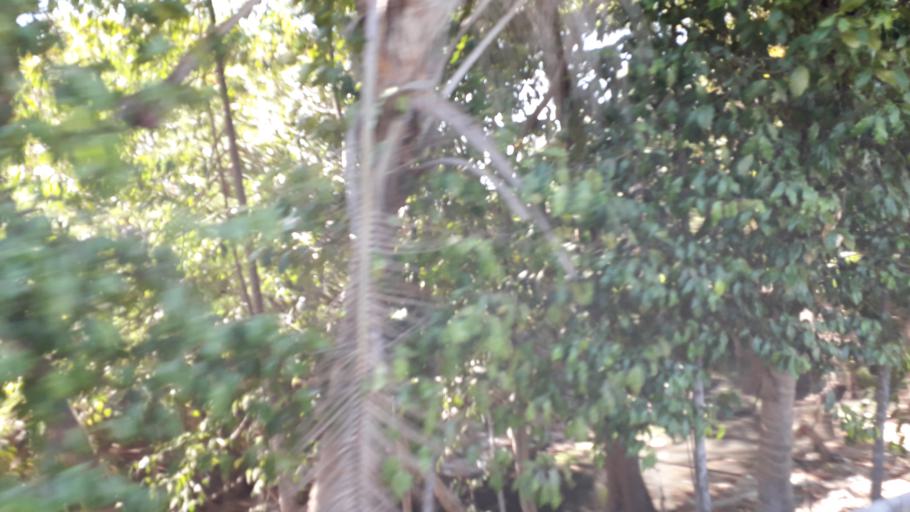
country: ID
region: Daerah Istimewa Yogyakarta
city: Pundong
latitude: -7.9586
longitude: 110.3235
